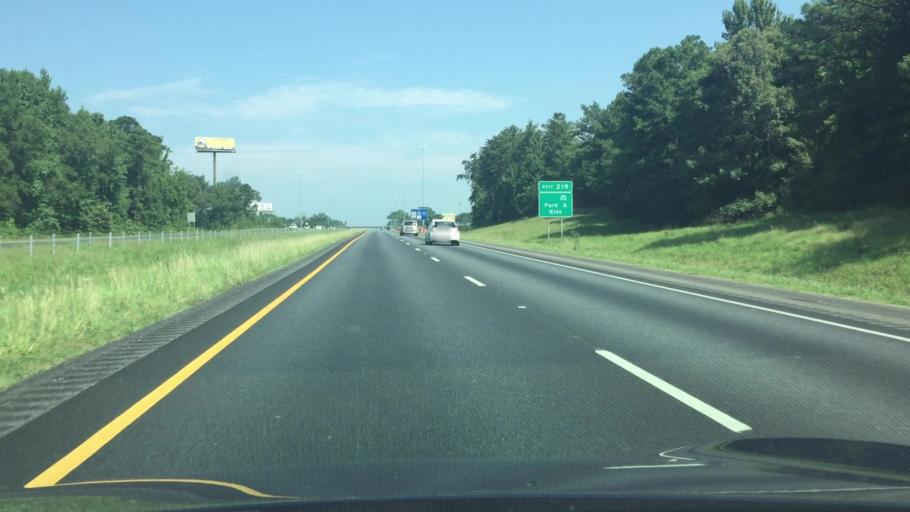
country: US
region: Alabama
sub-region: Chilton County
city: Jemison
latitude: 32.9725
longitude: -86.6830
